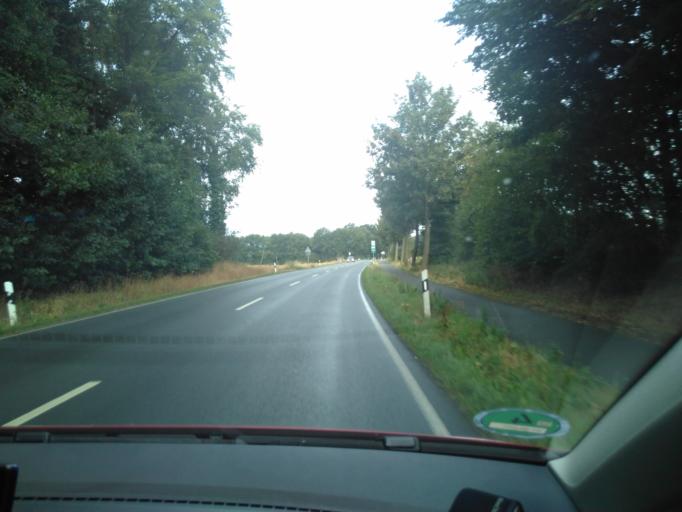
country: DE
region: North Rhine-Westphalia
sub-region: Regierungsbezirk Munster
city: Warendorf
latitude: 51.9698
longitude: 7.9663
